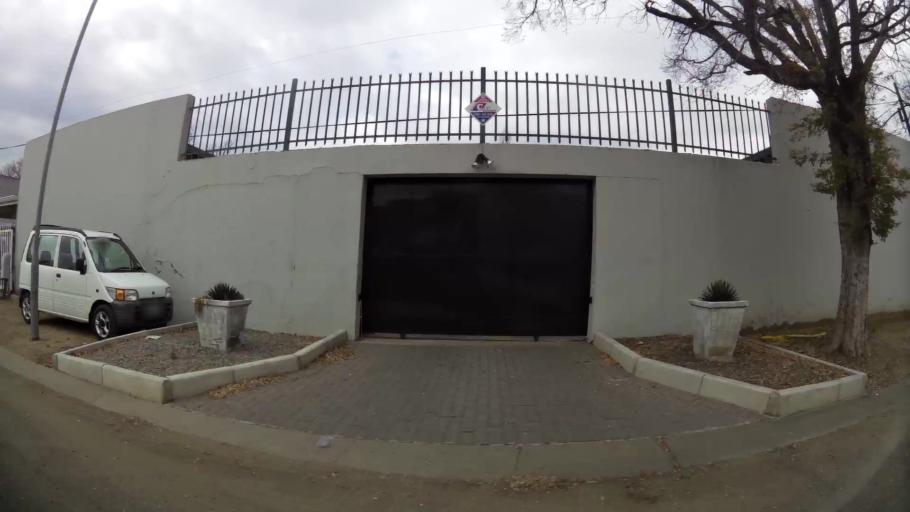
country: ZA
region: Orange Free State
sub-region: Fezile Dabi District Municipality
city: Kroonstad
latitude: -27.6713
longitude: 27.2346
